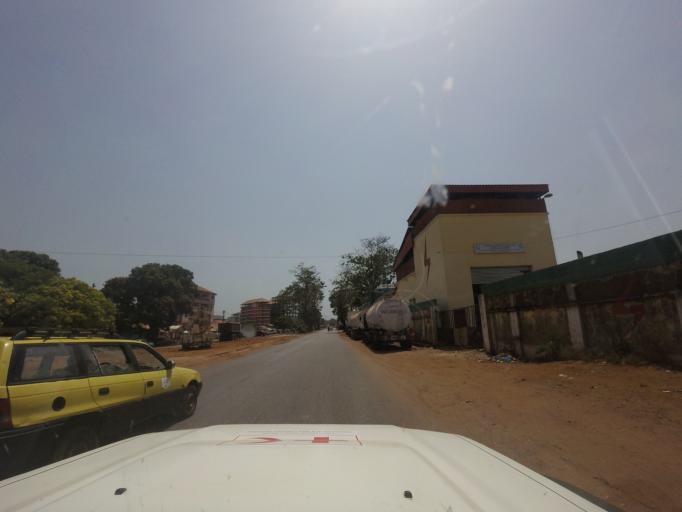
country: GN
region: Conakry
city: Camayenne
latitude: 9.5190
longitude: -13.6968
